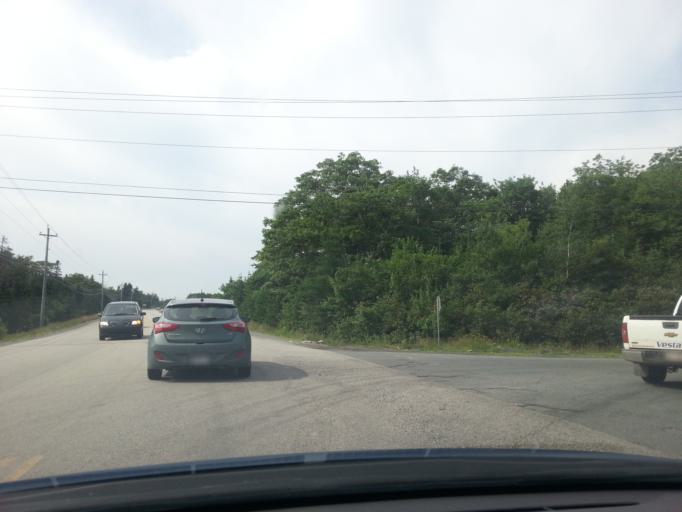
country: CA
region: Nova Scotia
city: Halifax
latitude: 44.6076
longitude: -63.6726
